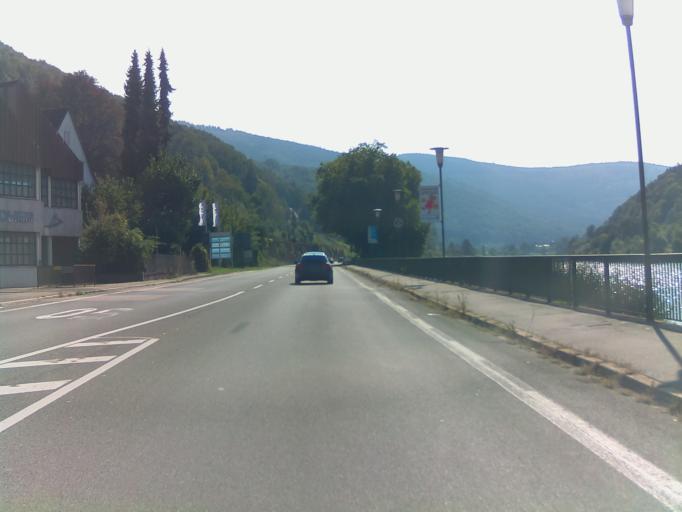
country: DE
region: Baden-Wuerttemberg
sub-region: Karlsruhe Region
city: Eberbach
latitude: 49.4587
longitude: 8.9889
